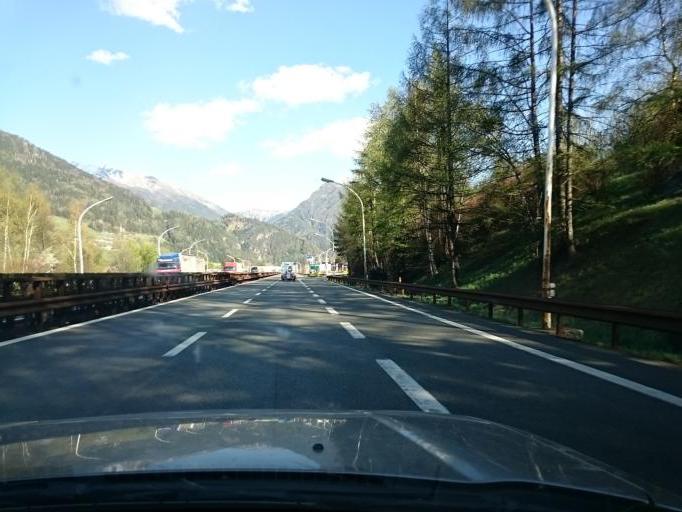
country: IT
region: Trentino-Alto Adige
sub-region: Bolzano
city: Campo di Trens
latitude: 46.8693
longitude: 11.4807
